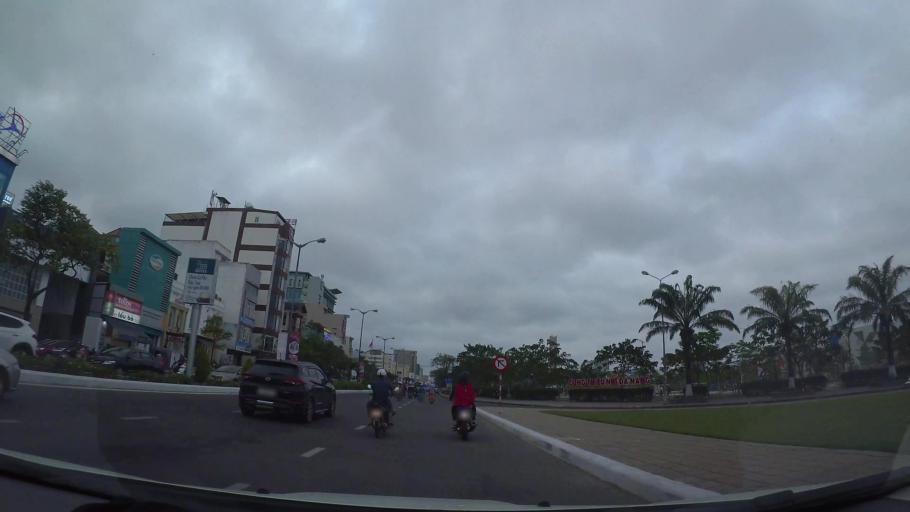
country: VN
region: Da Nang
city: Son Tra
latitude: 16.0380
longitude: 108.2237
